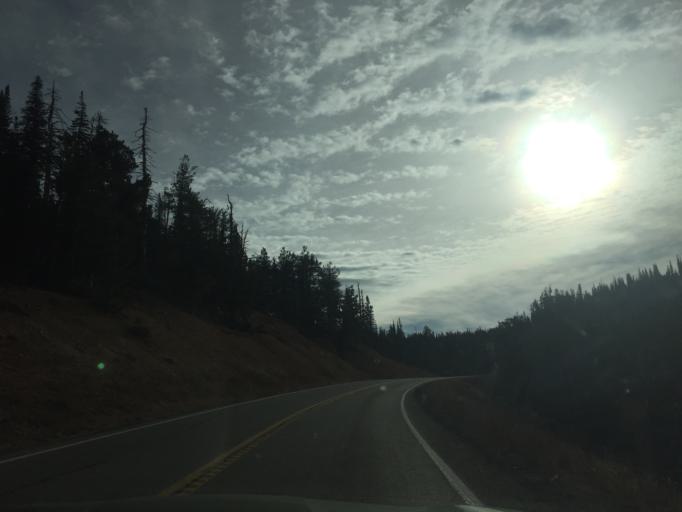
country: US
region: Utah
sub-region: Iron County
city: Cedar City
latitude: 37.5687
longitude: -112.8514
